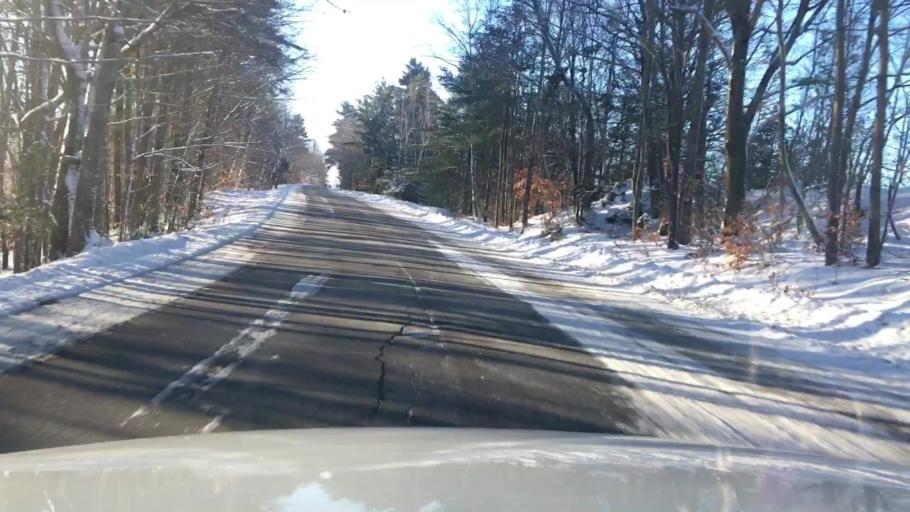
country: US
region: Maine
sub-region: Kennebec County
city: Belgrade
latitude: 44.4223
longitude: -69.8337
